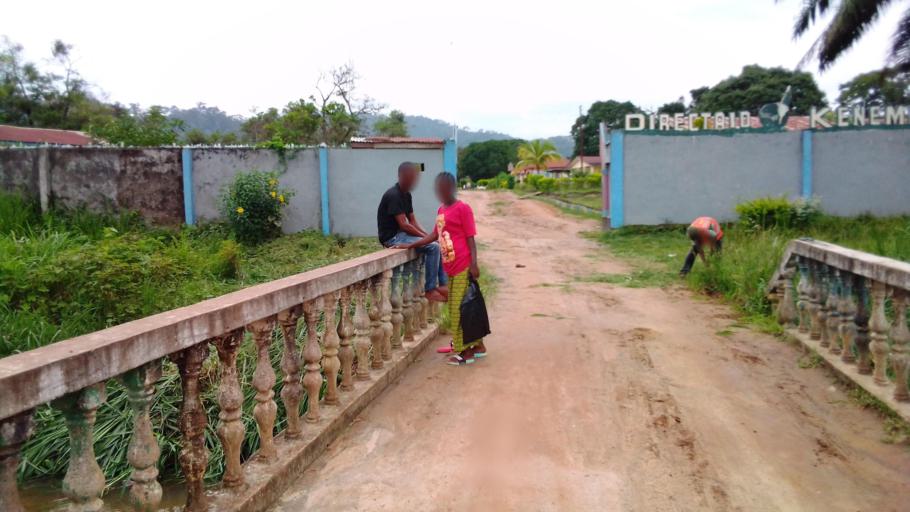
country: SL
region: Eastern Province
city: Kenema
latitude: 7.8611
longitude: -11.2018
